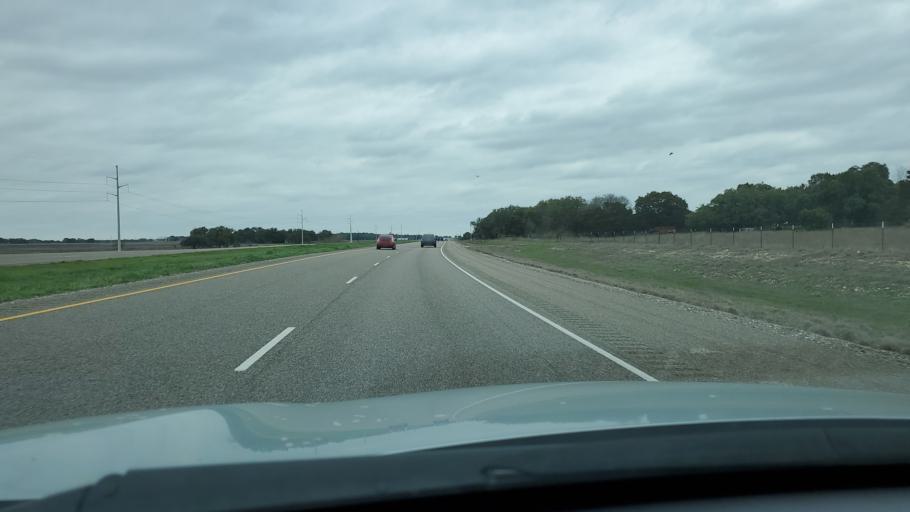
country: US
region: Texas
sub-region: Williamson County
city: Florence
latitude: 30.7732
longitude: -97.7584
